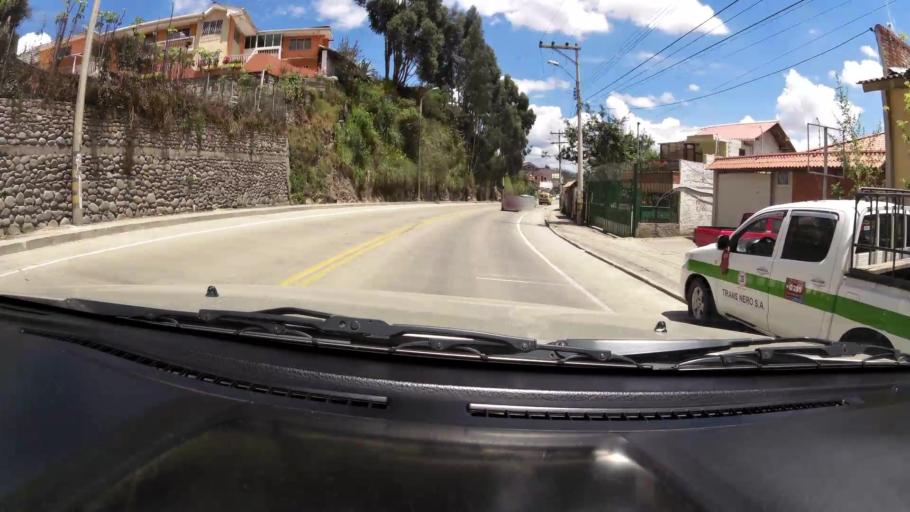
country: EC
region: Azuay
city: Cuenca
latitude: -2.9392
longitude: -79.0469
